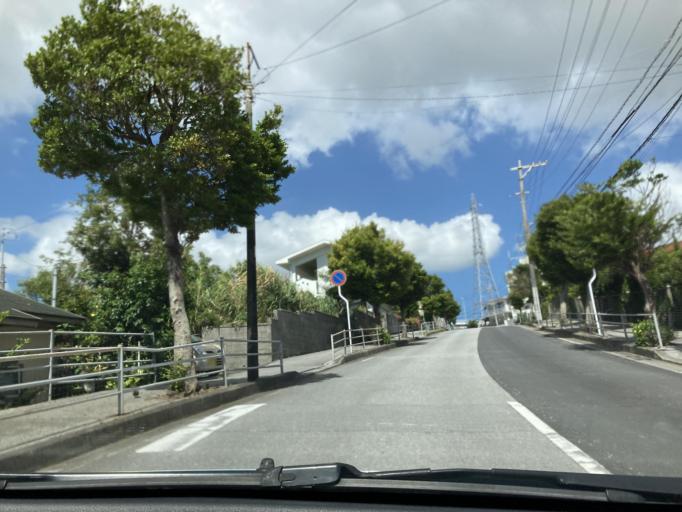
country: JP
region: Okinawa
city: Naha-shi
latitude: 26.2033
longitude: 127.7199
